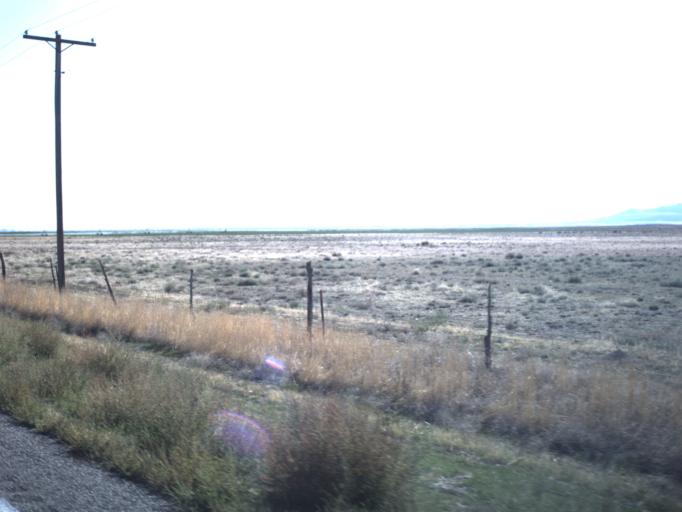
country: US
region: Utah
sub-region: Millard County
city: Delta
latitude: 39.1984
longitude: -112.4100
